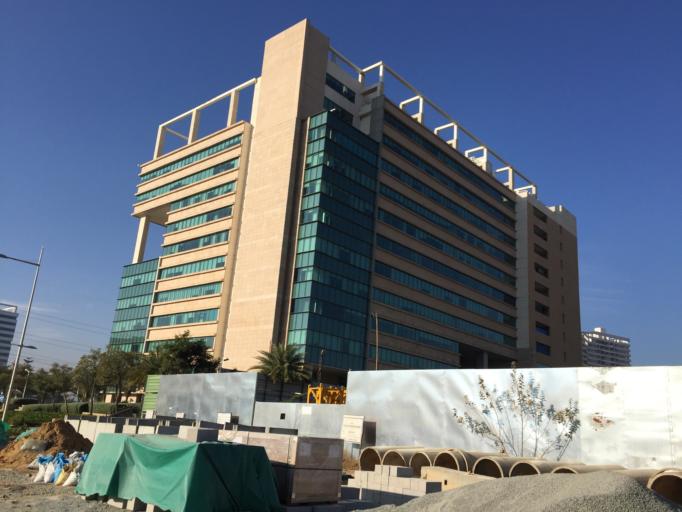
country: IN
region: Karnataka
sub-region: Bangalore Urban
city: Yelahanka
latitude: 13.0533
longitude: 77.6201
